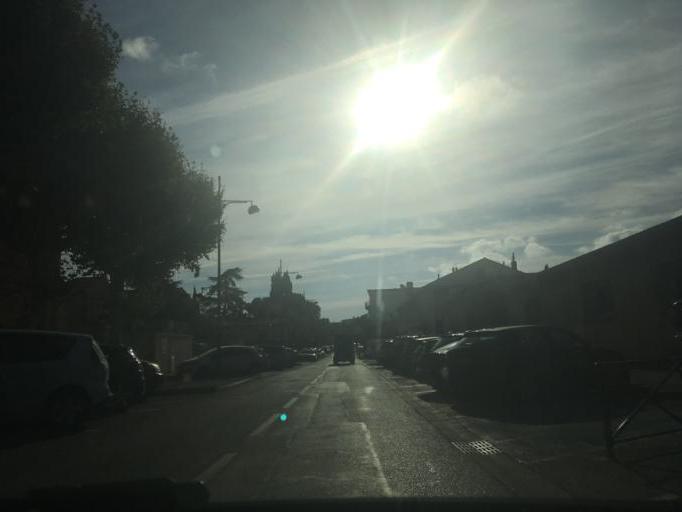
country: FR
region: Provence-Alpes-Cote d'Azur
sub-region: Departement du Var
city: Draguignan
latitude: 43.5407
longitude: 6.4580
